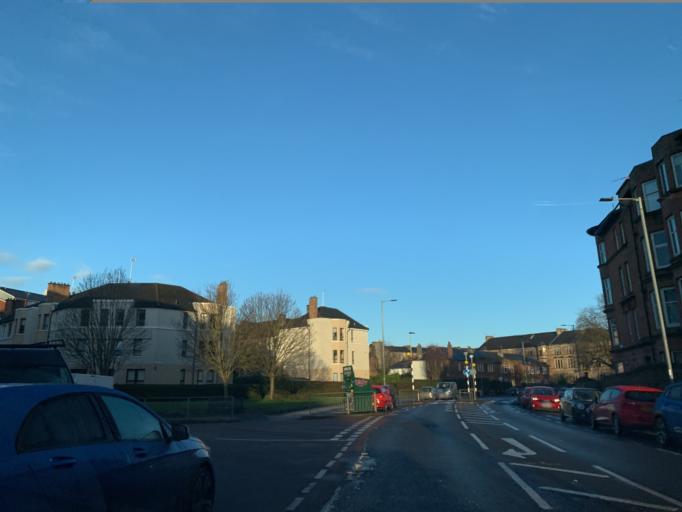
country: GB
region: Scotland
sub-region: East Renfrewshire
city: Giffnock
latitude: 55.8243
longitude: -4.2829
